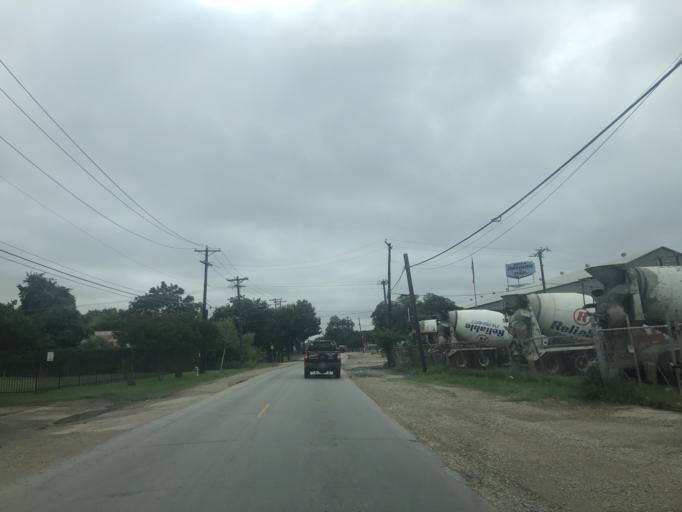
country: US
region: Texas
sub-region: Dallas County
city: Cockrell Hill
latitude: 32.7728
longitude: -96.8555
